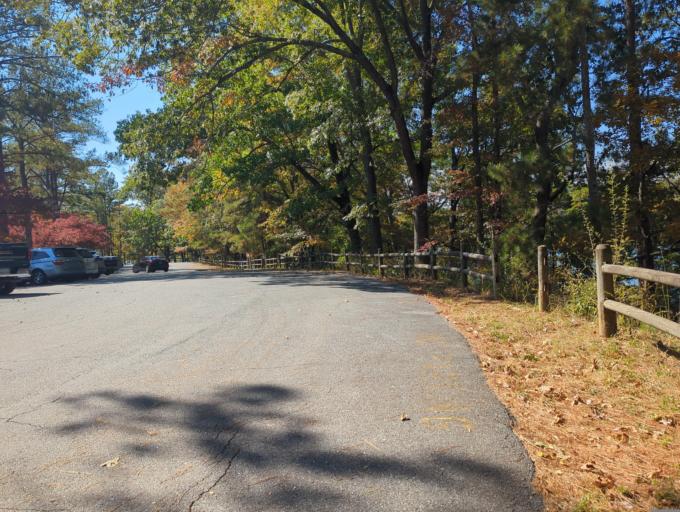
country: US
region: Georgia
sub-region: Bartow County
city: Emerson
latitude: 34.1510
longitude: -84.7157
